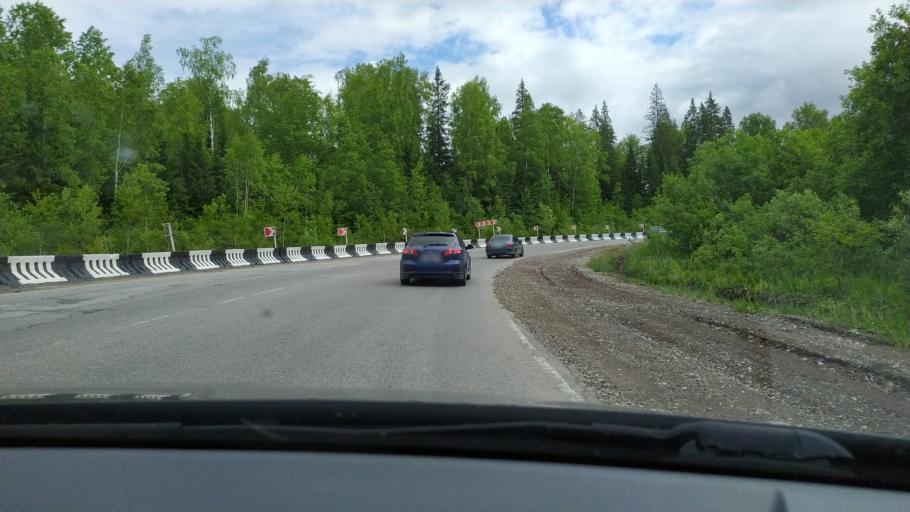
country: RU
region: Perm
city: Gremyachinsk
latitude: 58.4420
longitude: 57.8853
